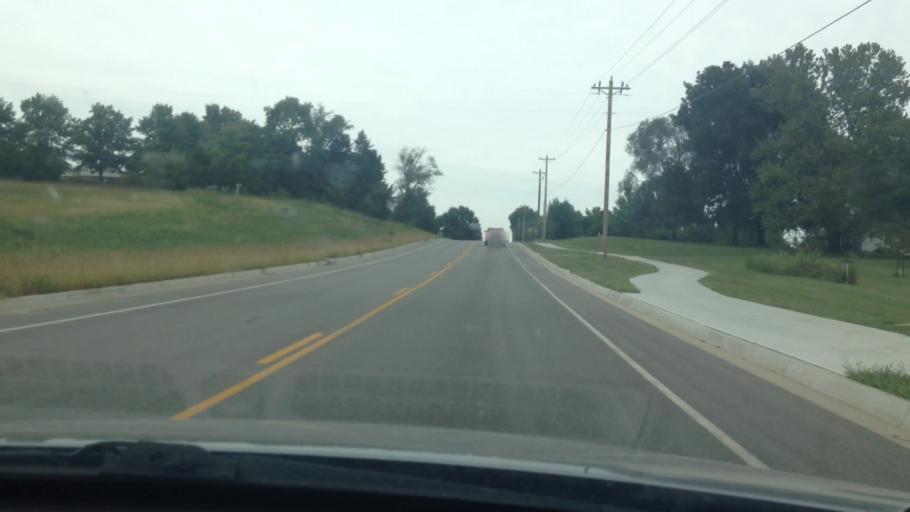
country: US
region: Missouri
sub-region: Platte County
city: Platte City
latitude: 39.3452
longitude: -94.7793
